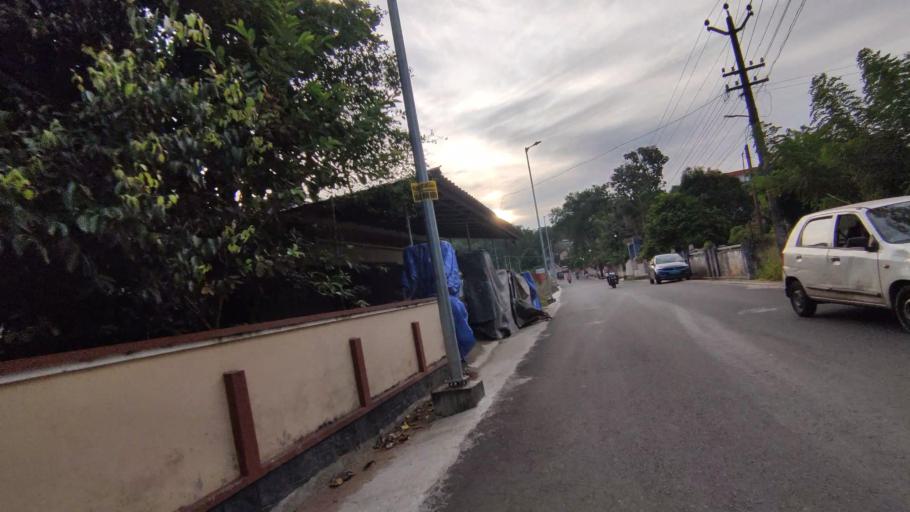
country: IN
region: Kerala
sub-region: Kottayam
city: Kottayam
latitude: 9.6424
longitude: 76.5112
